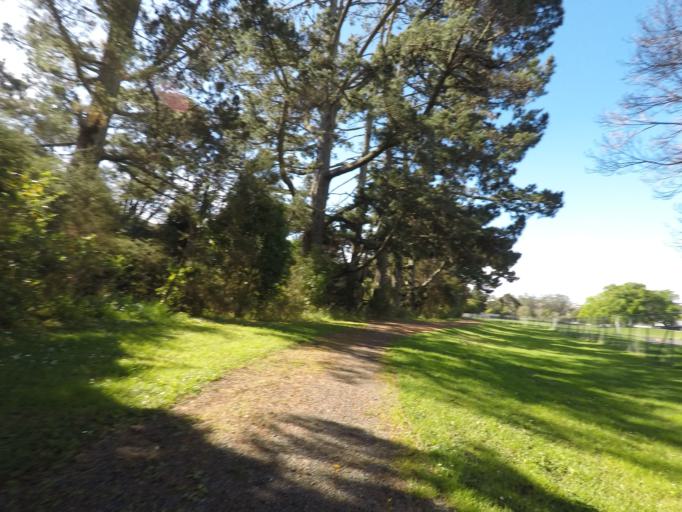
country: NZ
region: Auckland
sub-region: Auckland
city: Rosebank
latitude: -36.8559
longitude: 174.6002
